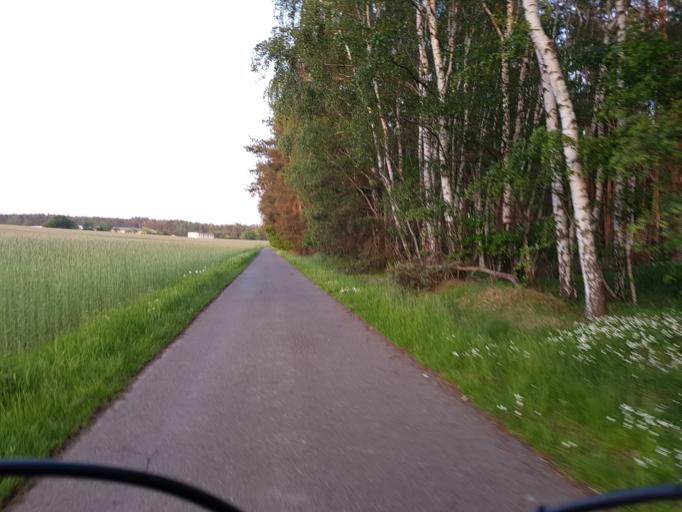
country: DE
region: Brandenburg
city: Bad Liebenwerda
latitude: 51.5553
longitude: 13.4140
